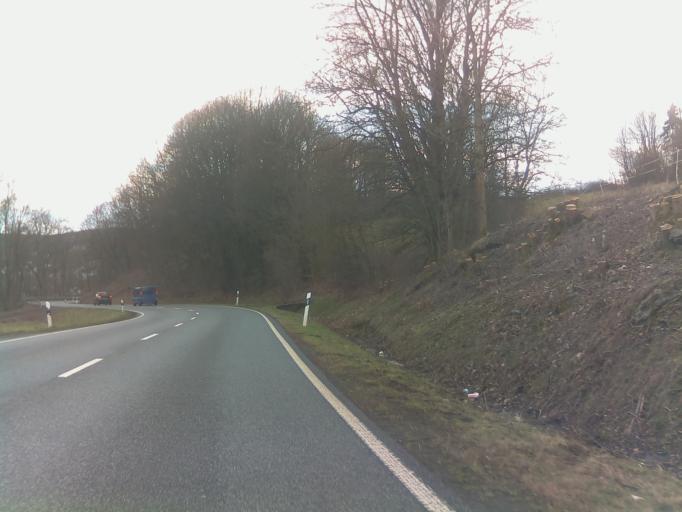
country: DE
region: Hesse
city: Gedern
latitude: 50.4331
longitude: 9.1998
